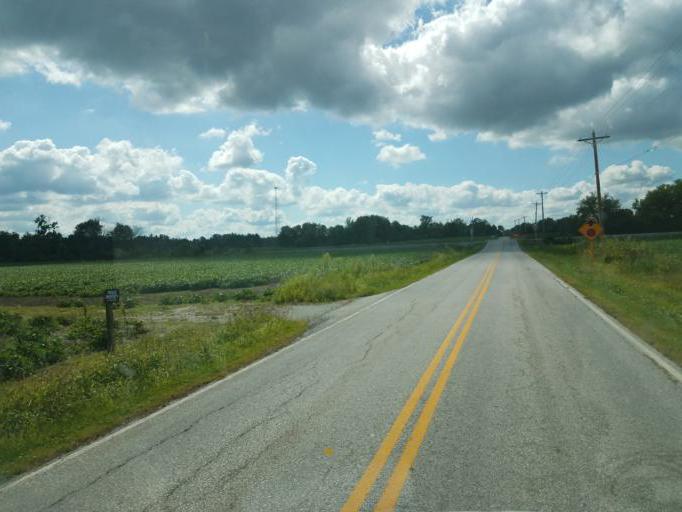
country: US
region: Ohio
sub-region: Medina County
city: Lodi
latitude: 41.1041
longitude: -82.0944
